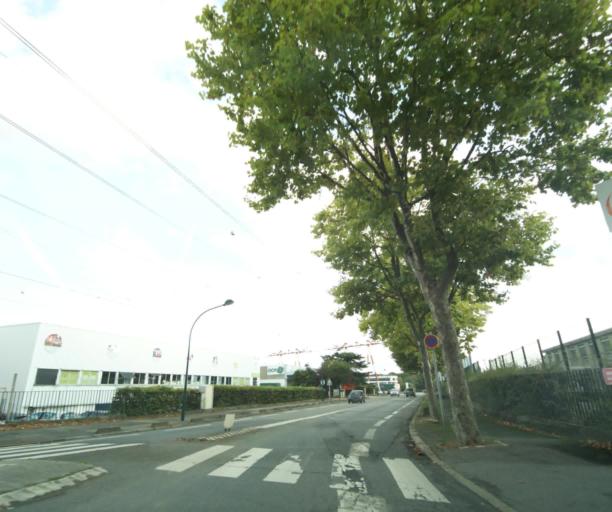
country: FR
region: Ile-de-France
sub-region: Departement des Hauts-de-Seine
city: Chatenay-Malabry
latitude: 48.7768
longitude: 2.2456
